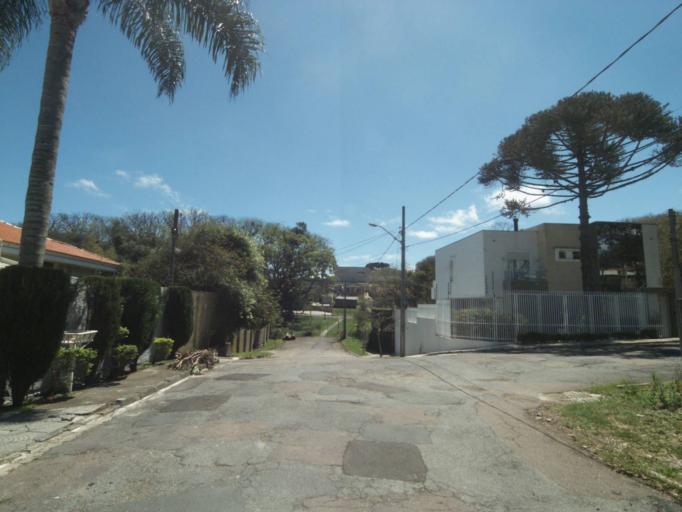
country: BR
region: Parana
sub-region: Curitiba
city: Curitiba
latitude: -25.3843
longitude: -49.2632
